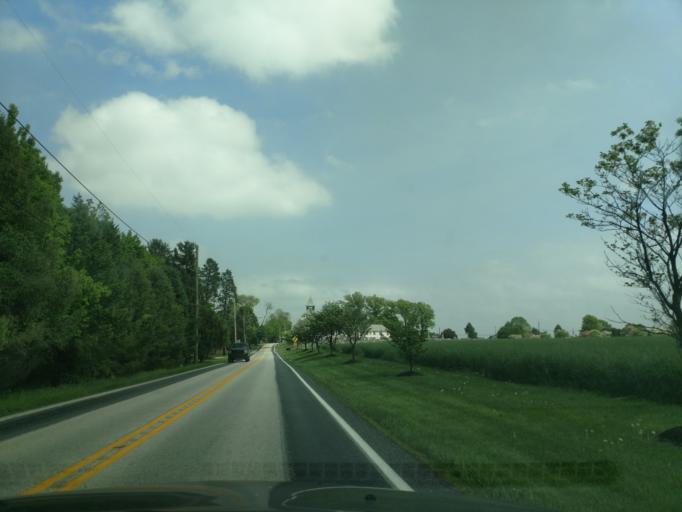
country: US
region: Pennsylvania
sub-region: Chester County
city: Kenilworth
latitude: 40.1772
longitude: -75.6279
